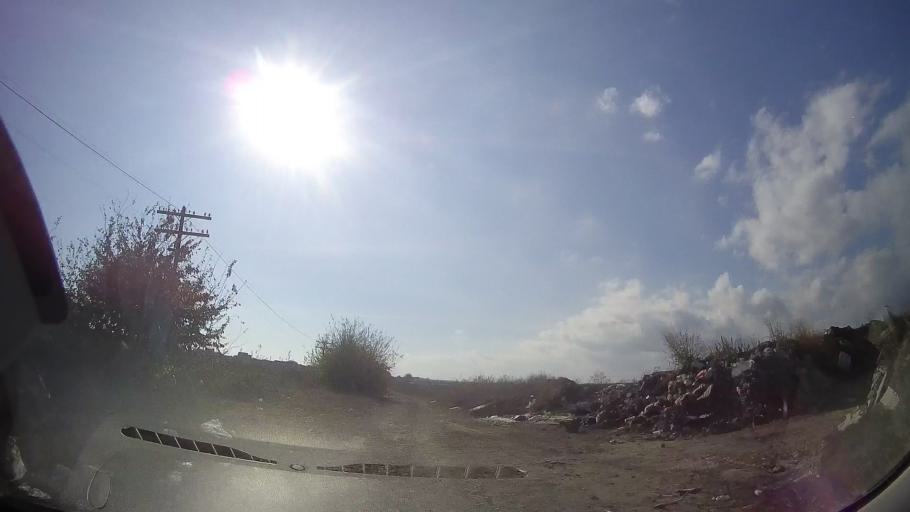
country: RO
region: Constanta
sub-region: Comuna Costinesti
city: Costinesti
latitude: 43.9676
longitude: 28.6411
